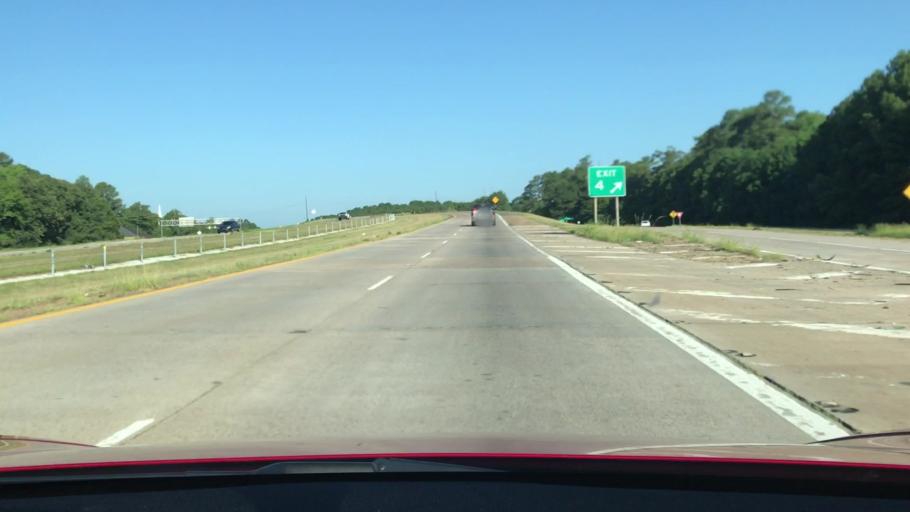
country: US
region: Louisiana
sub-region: Bossier Parish
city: Bossier City
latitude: 32.4168
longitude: -93.7930
